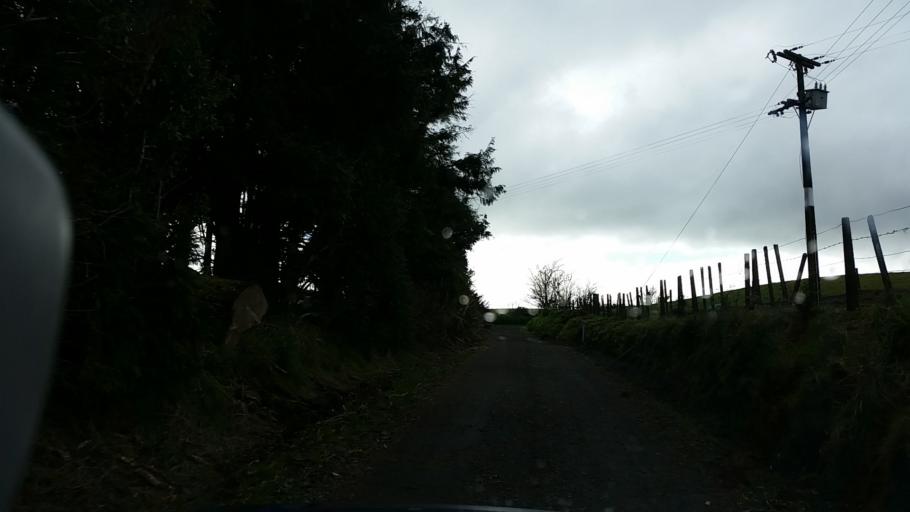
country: NZ
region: Taranaki
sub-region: South Taranaki District
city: Eltham
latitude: -39.2767
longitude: 174.3394
